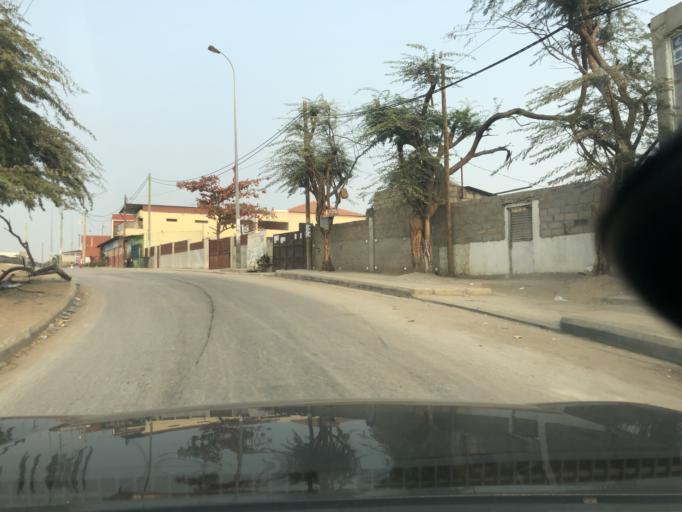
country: AO
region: Luanda
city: Luanda
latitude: -8.8796
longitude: 13.1891
